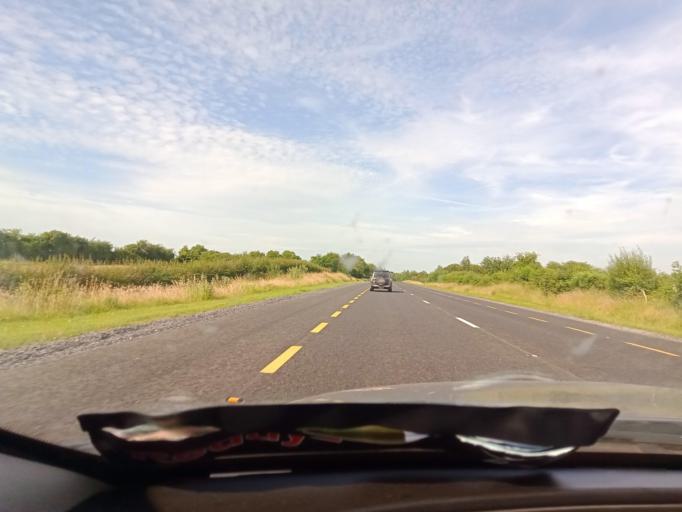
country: IE
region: Leinster
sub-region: An Iarmhi
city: An Muileann gCearr
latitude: 53.4867
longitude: -7.3417
